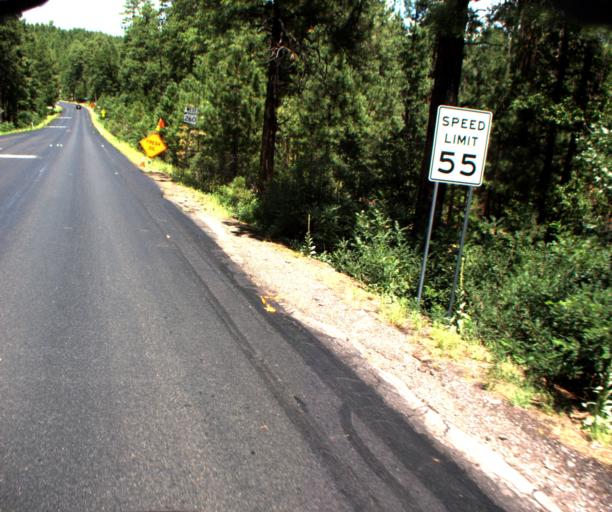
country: US
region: Arizona
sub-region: Gila County
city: Pine
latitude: 34.4547
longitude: -111.4386
